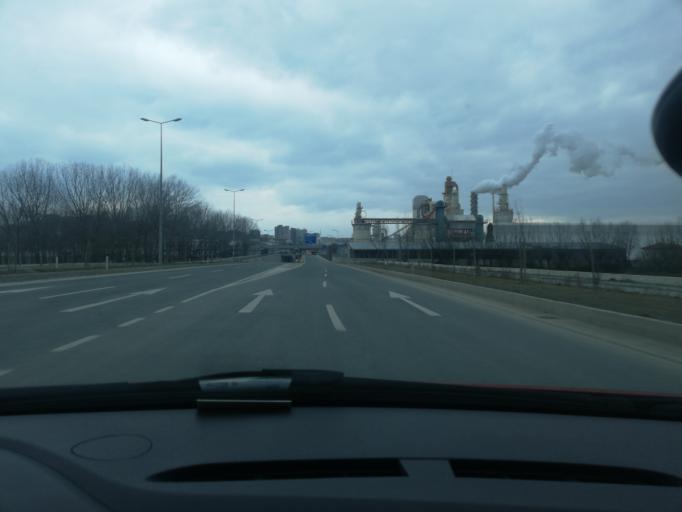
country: TR
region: Kastamonu
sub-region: Cide
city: Kastamonu
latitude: 41.4138
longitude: 33.8016
